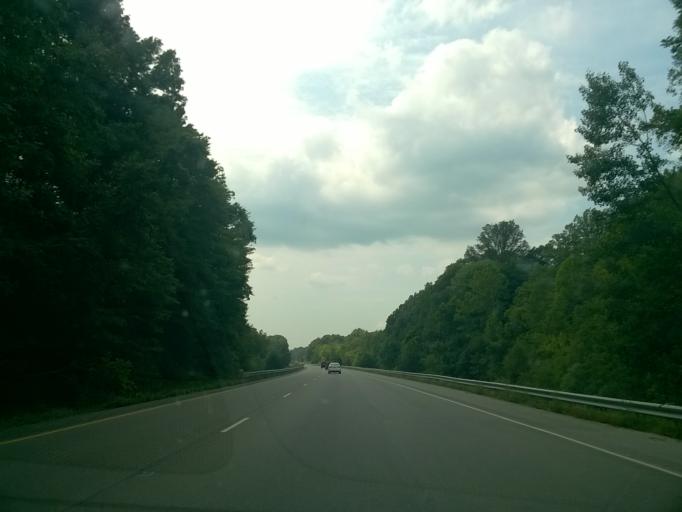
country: US
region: Indiana
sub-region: Putnam County
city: Cloverdale
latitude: 39.5255
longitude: -86.8855
